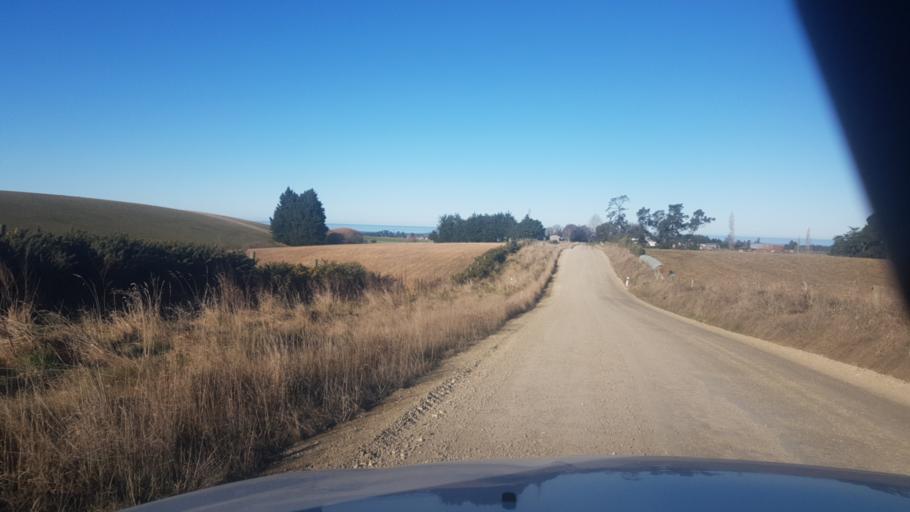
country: NZ
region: Canterbury
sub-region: Timaru District
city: Pleasant Point
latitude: -44.3701
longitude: 171.0731
